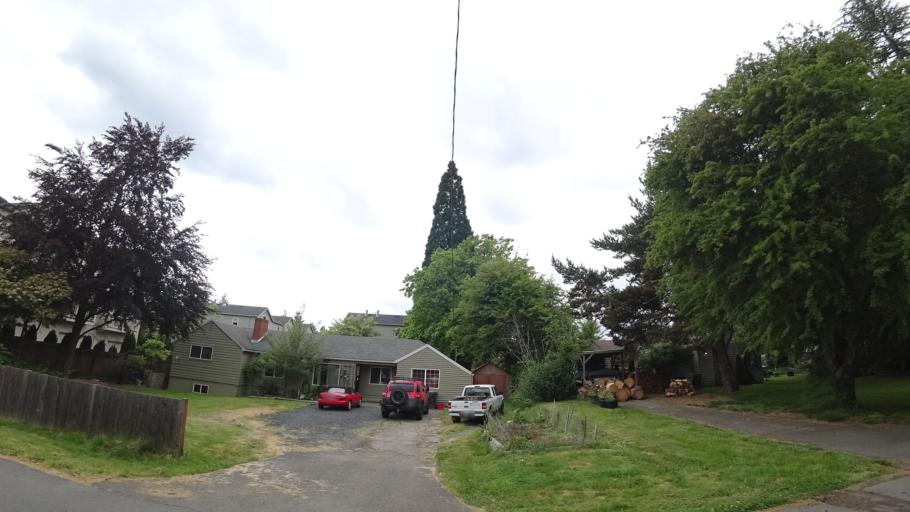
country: US
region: Oregon
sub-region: Washington County
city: West Slope
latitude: 45.4941
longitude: -122.7825
